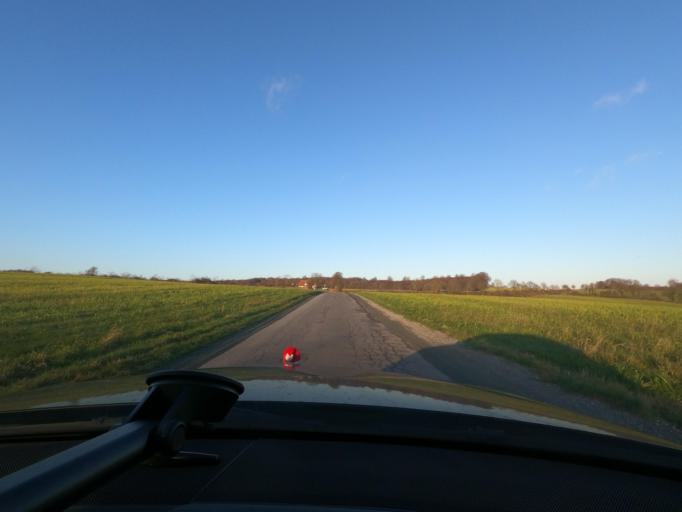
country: DK
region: South Denmark
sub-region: Sonderborg Kommune
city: Broager
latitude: 54.9036
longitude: 9.6969
